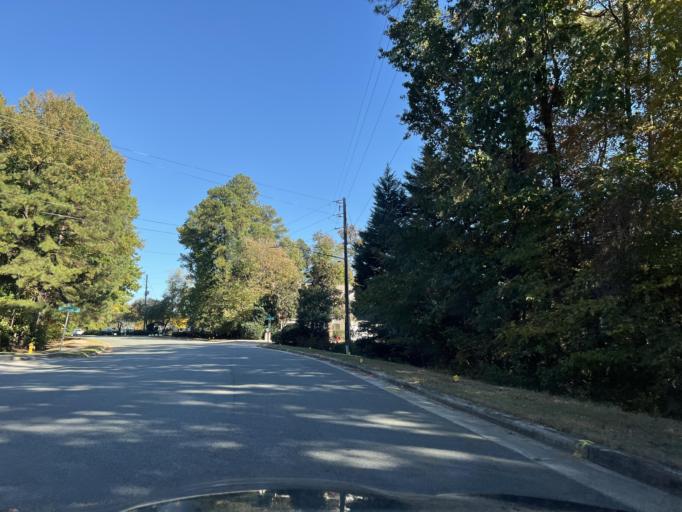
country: US
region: North Carolina
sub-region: Wake County
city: West Raleigh
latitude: 35.8767
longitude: -78.5948
